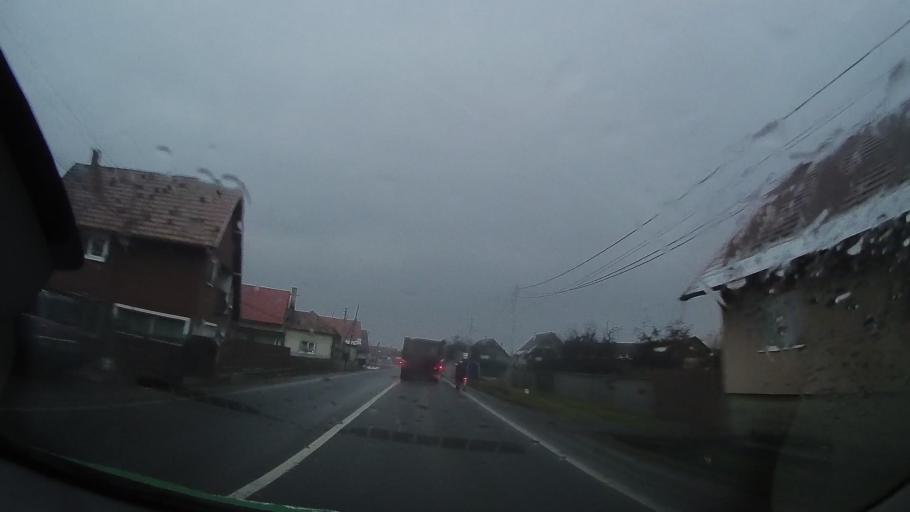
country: RO
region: Harghita
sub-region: Comuna Lazarea
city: Lazarea
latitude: 46.7549
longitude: 25.5192
